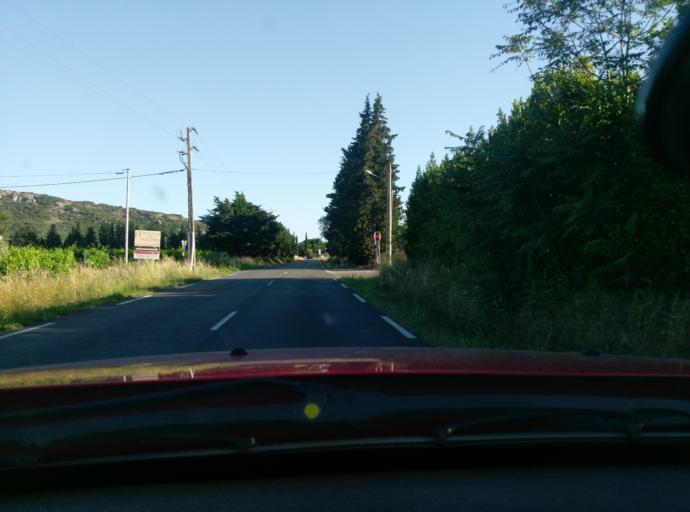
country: FR
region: Languedoc-Roussillon
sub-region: Departement du Gard
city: Sernhac
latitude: 43.9228
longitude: 4.5631
